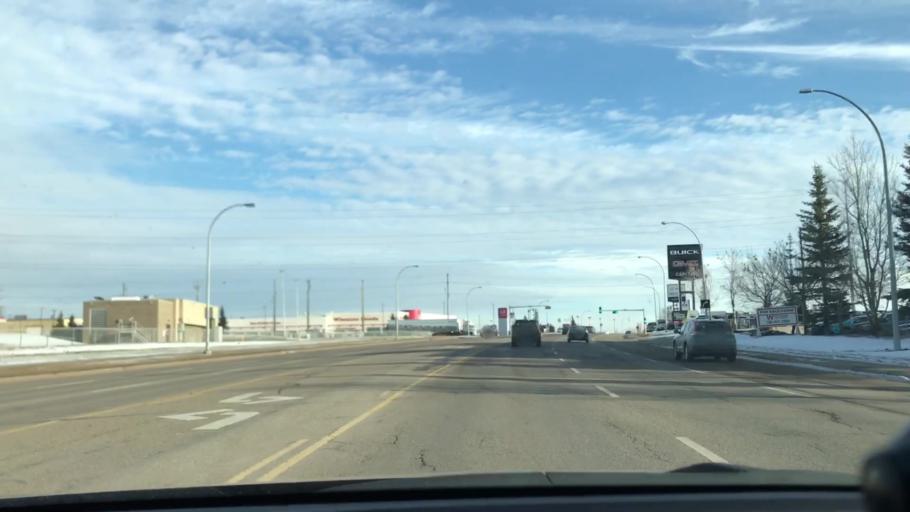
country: CA
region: Alberta
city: Edmonton
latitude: 53.4676
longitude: -113.4827
